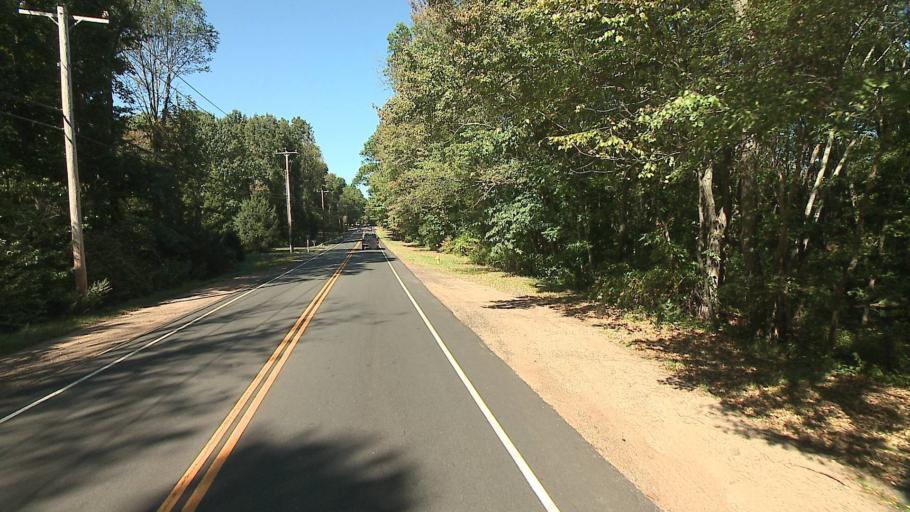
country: US
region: Connecticut
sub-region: New Haven County
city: Orange
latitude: 41.2901
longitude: -73.0138
